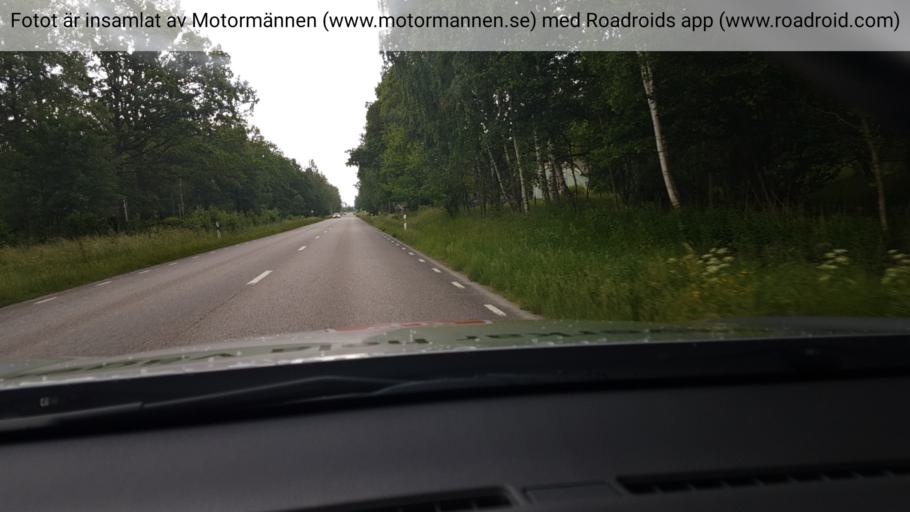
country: SE
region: Vaestra Goetaland
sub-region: Hjo Kommun
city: Hjo
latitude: 58.1582
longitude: 14.2118
